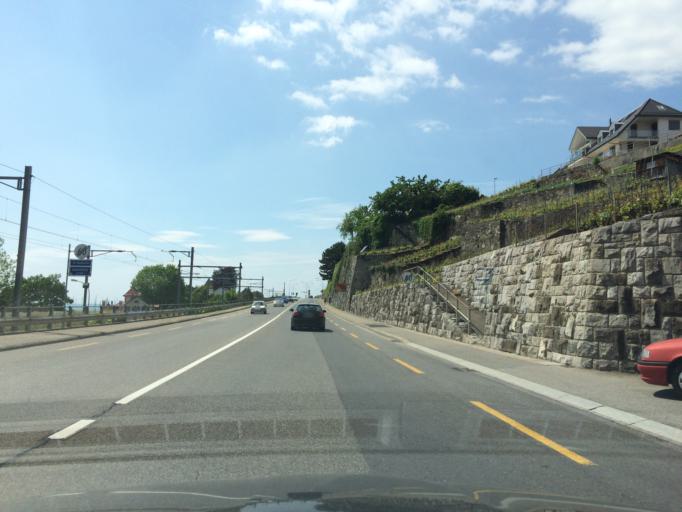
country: CH
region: Vaud
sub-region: Riviera-Pays-d'Enhaut District
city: Chardonne
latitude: 46.4704
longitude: 6.8196
